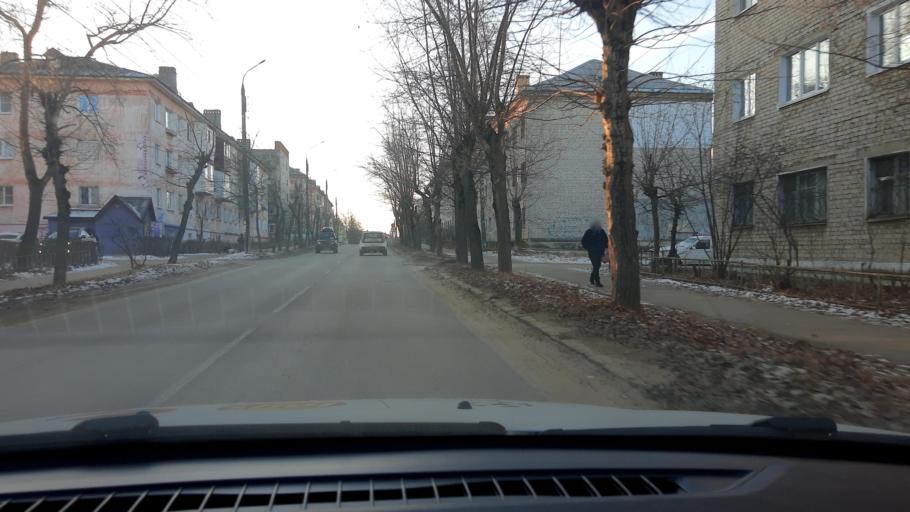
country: RU
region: Nizjnij Novgorod
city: Dzerzhinsk
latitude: 56.2484
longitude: 43.4566
